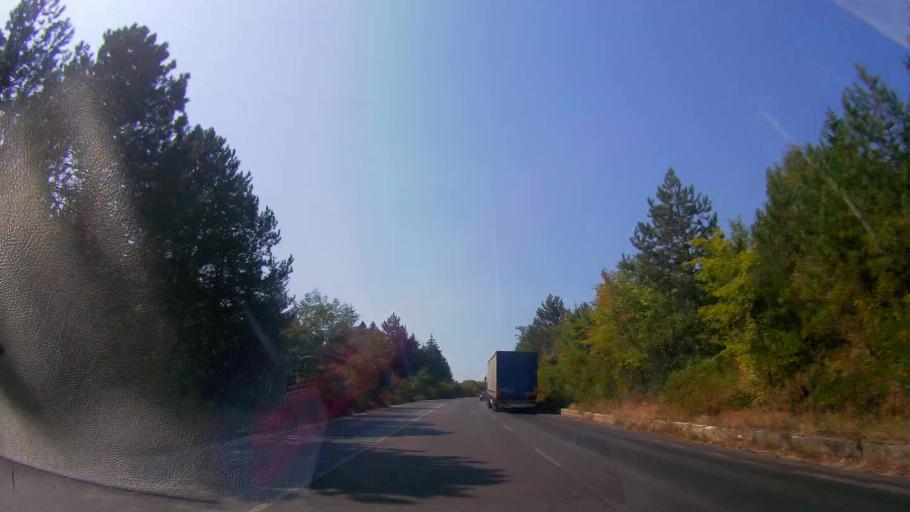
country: BG
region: Ruse
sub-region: Obshtina Vetovo
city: Senovo
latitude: 43.5608
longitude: 26.3748
